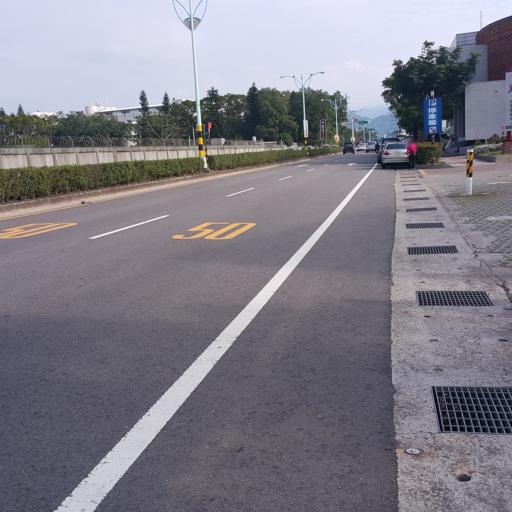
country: TW
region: Taiwan
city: Daxi
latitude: 24.8464
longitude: 121.2337
